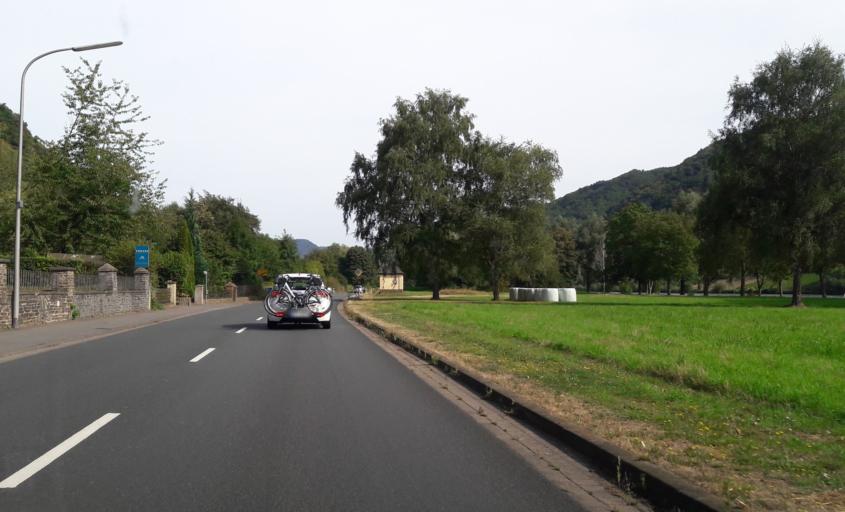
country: DE
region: Rheinland-Pfalz
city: Bullay
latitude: 50.0597
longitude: 7.1283
